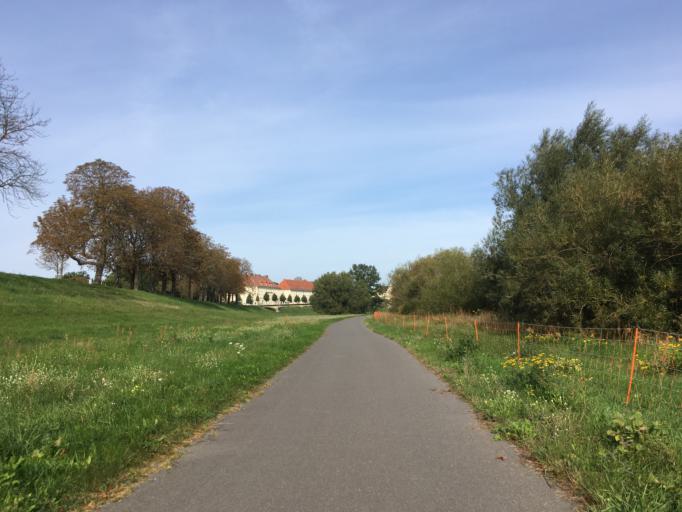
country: DE
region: Brandenburg
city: Forst
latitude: 51.7383
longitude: 14.6597
